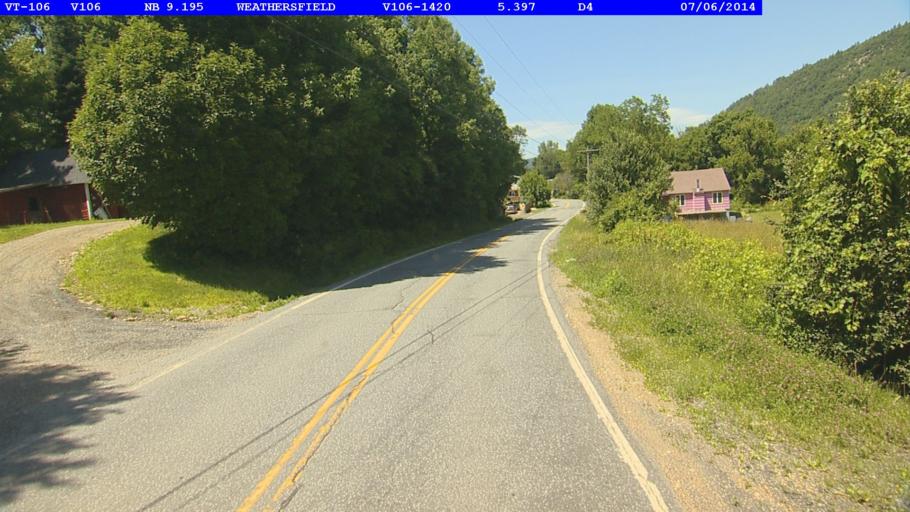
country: US
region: Vermont
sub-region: Windsor County
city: Springfield
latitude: 43.4148
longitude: -72.5170
